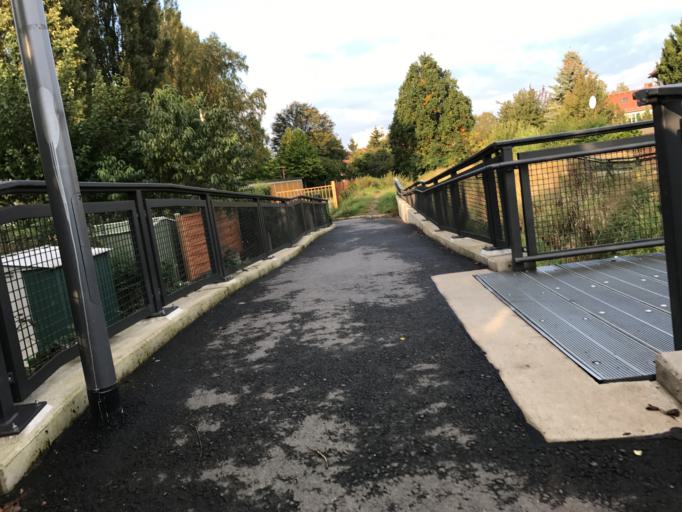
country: DE
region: Saxony
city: Albertstadt
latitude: 51.0339
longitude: 13.7958
